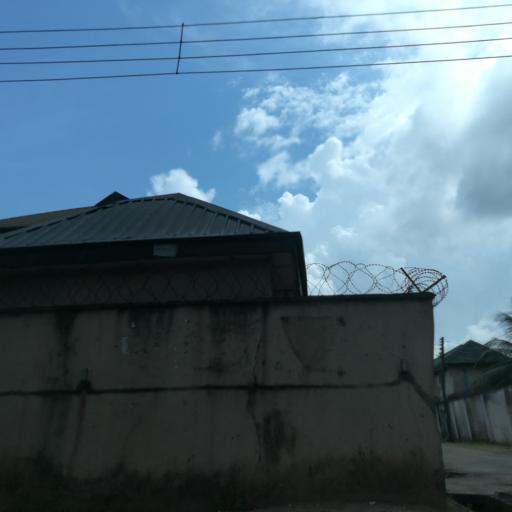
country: NG
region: Rivers
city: Port Harcourt
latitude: 4.8113
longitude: 7.0619
